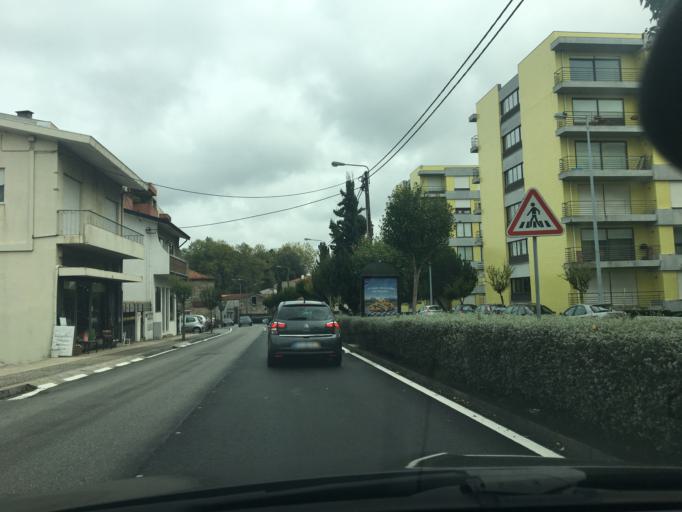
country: PT
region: Porto
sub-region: Maia
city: Anta
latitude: 41.2639
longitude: -8.6147
